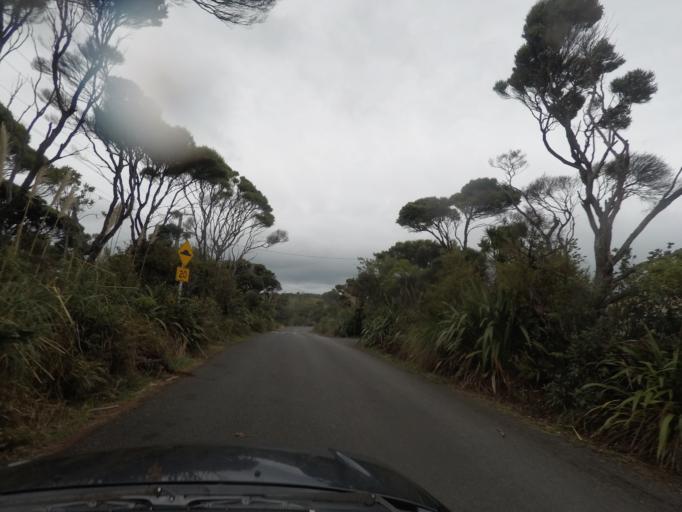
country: NZ
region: Auckland
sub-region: Auckland
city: Muriwai Beach
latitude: -36.9694
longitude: 174.4753
